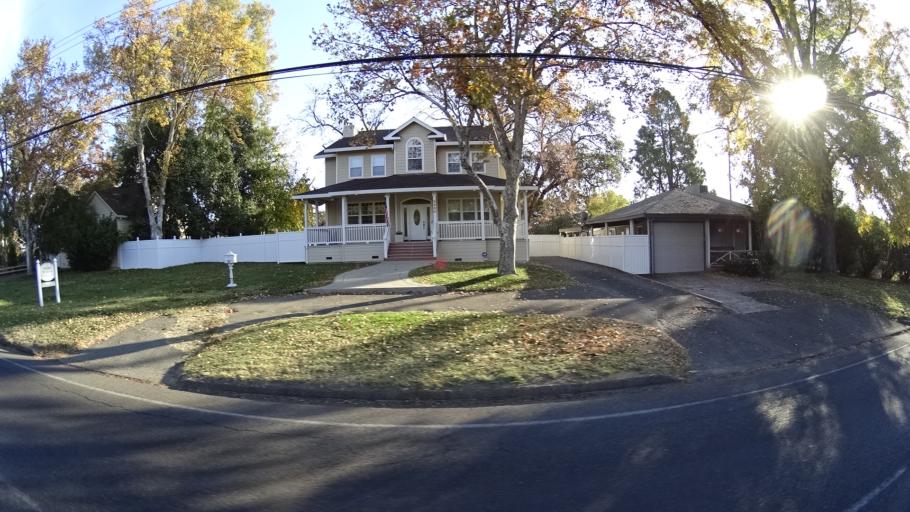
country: US
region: California
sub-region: Sacramento County
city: Citrus Heights
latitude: 38.7207
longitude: -121.2719
